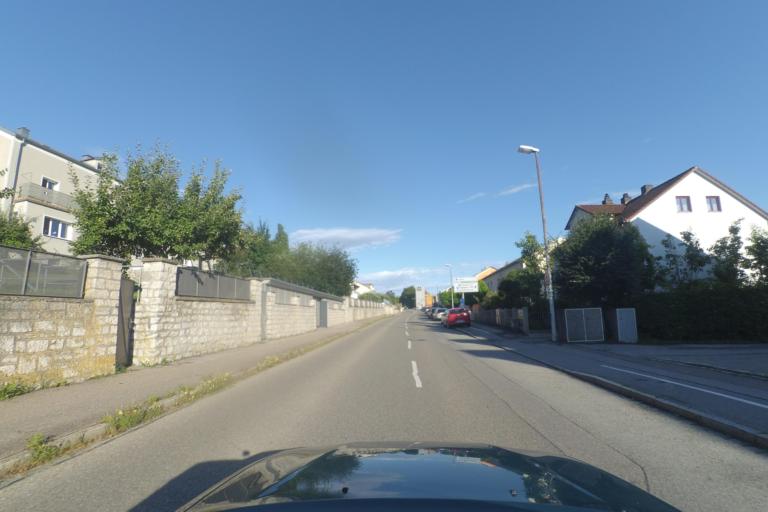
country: DE
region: Bavaria
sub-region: Upper Bavaria
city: Eichstaett
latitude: 48.8867
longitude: 11.1998
